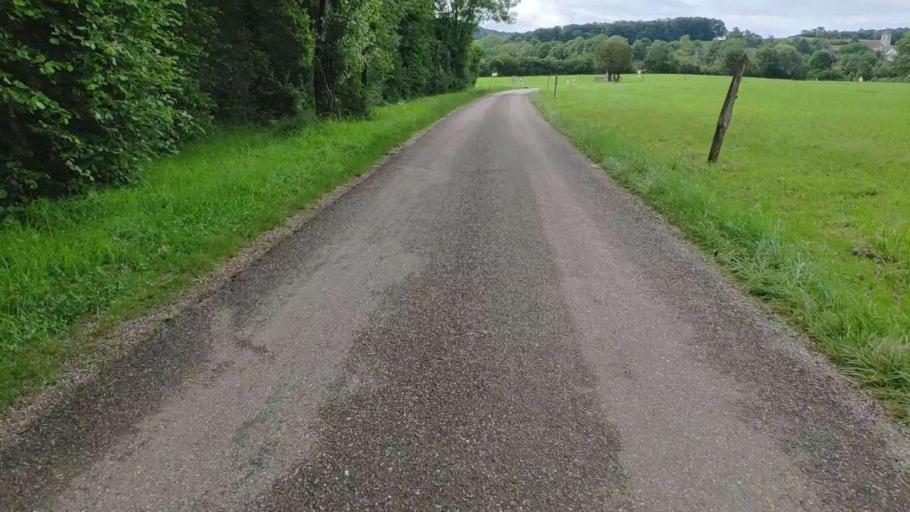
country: FR
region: Franche-Comte
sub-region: Departement du Jura
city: Poligny
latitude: 46.8018
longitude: 5.6013
